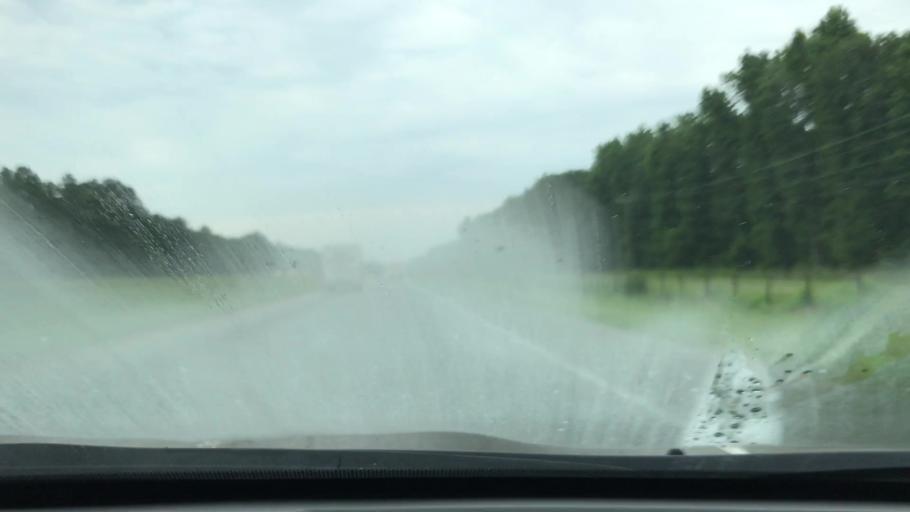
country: US
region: South Carolina
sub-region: Jasper County
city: Ridgeland
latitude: 32.5543
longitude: -80.9469
